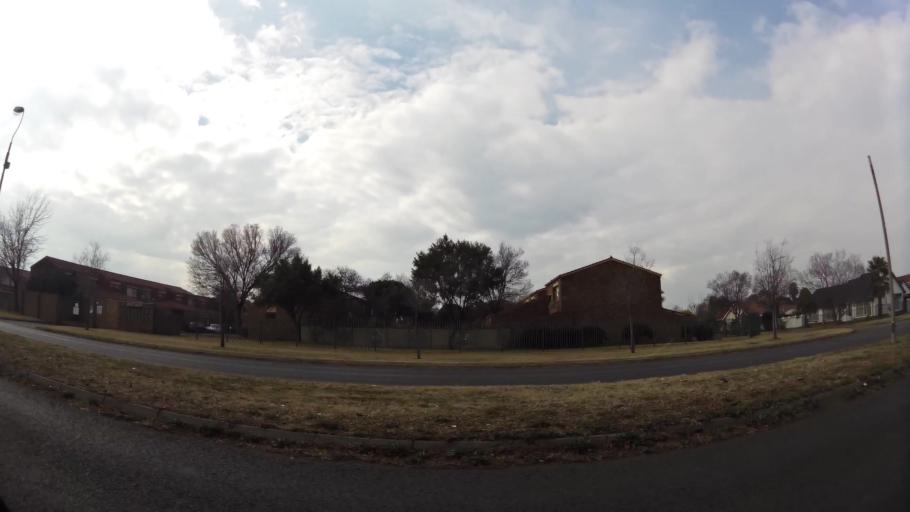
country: ZA
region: Gauteng
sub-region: Sedibeng District Municipality
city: Vanderbijlpark
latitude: -26.6943
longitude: 27.8474
